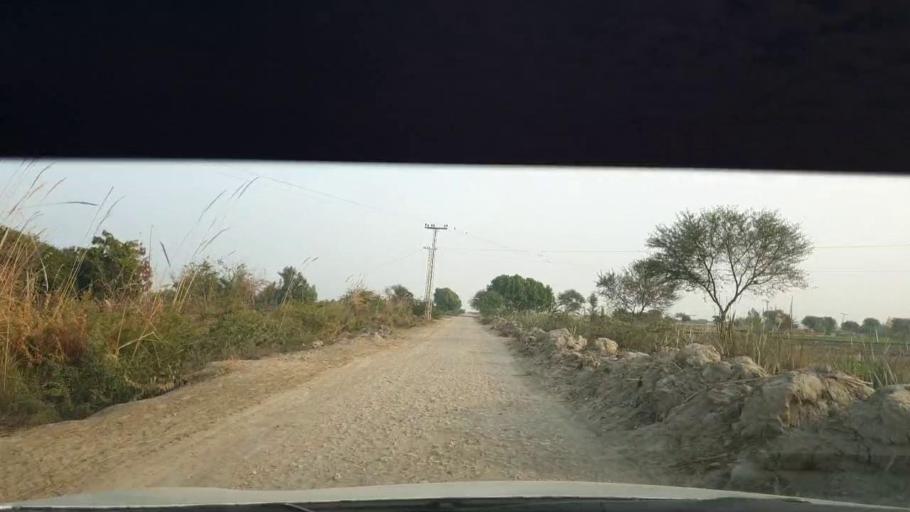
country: PK
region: Sindh
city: Berani
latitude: 25.7282
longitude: 68.9714
